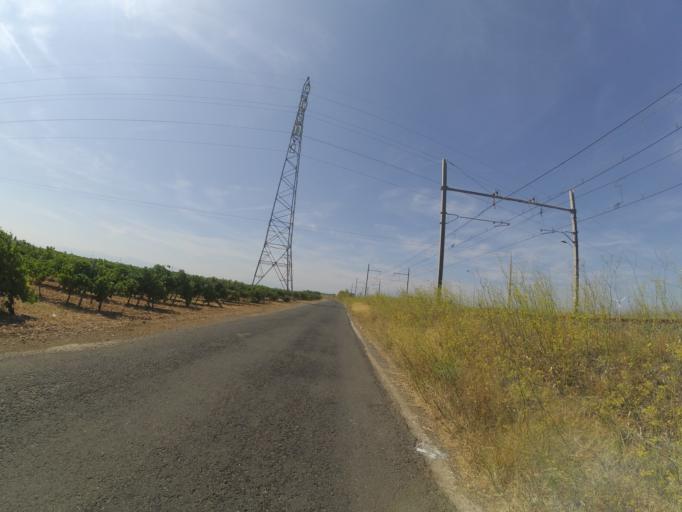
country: FR
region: Languedoc-Roussillon
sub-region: Departement des Pyrenees-Orientales
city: Salses-le-Chateau
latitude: 42.7993
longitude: 2.9018
